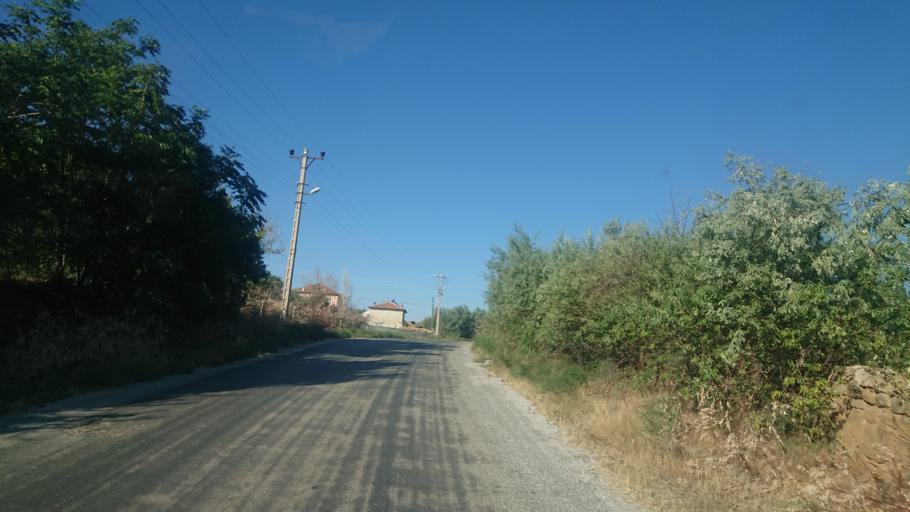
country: TR
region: Ankara
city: Sereflikochisar
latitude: 38.7692
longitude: 33.7023
